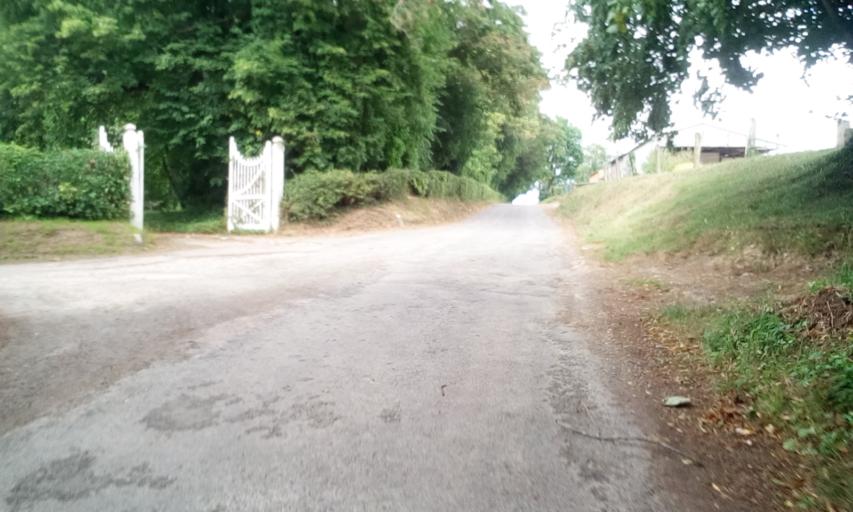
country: FR
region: Lower Normandy
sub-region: Departement du Calvados
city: Tilly-sur-Seulles
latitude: 49.2171
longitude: -0.6233
